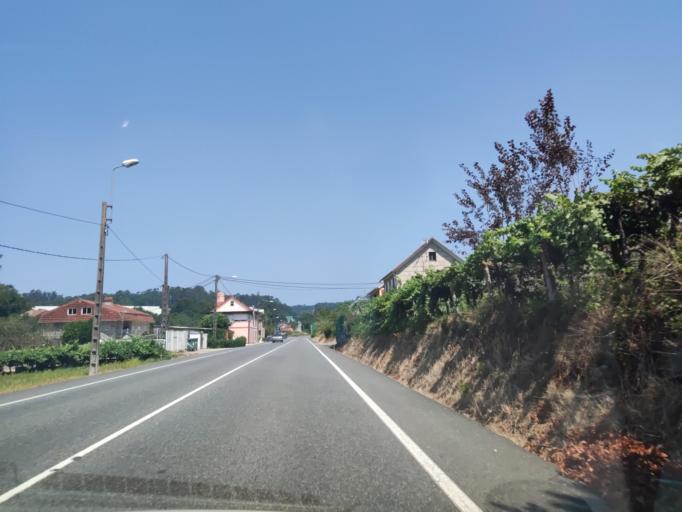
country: ES
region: Galicia
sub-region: Provincia de Pontevedra
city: Redondela
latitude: 42.2323
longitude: -8.5963
